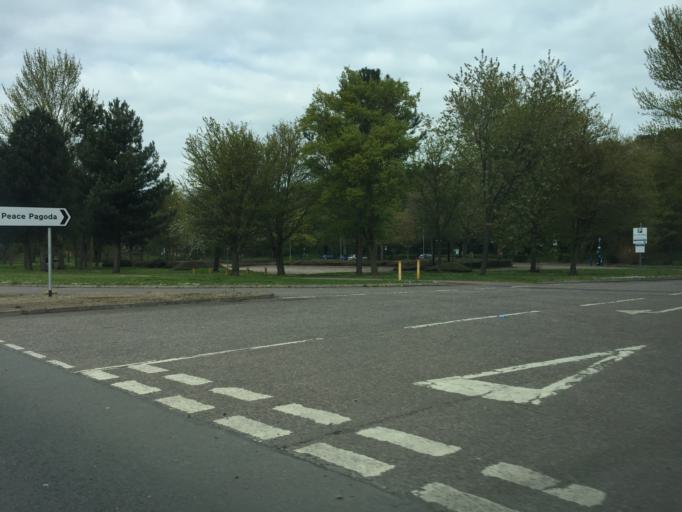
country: GB
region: England
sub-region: Milton Keynes
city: Milton Keynes
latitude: 52.0561
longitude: -0.7285
